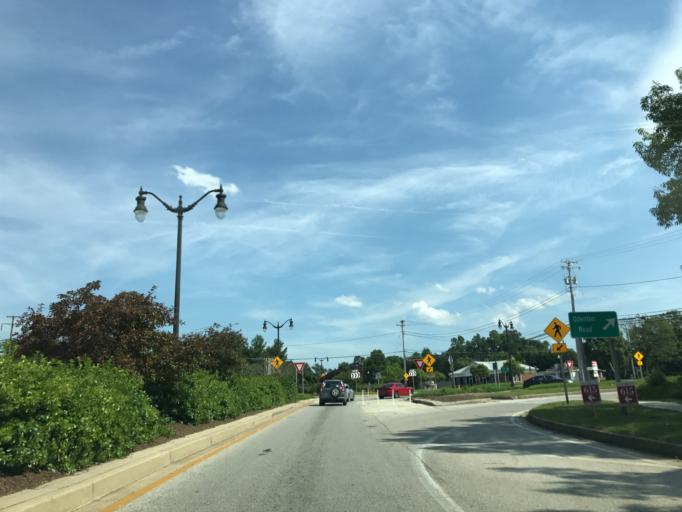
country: US
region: Maryland
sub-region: Anne Arundel County
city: Odenton
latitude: 39.0789
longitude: -76.6855
